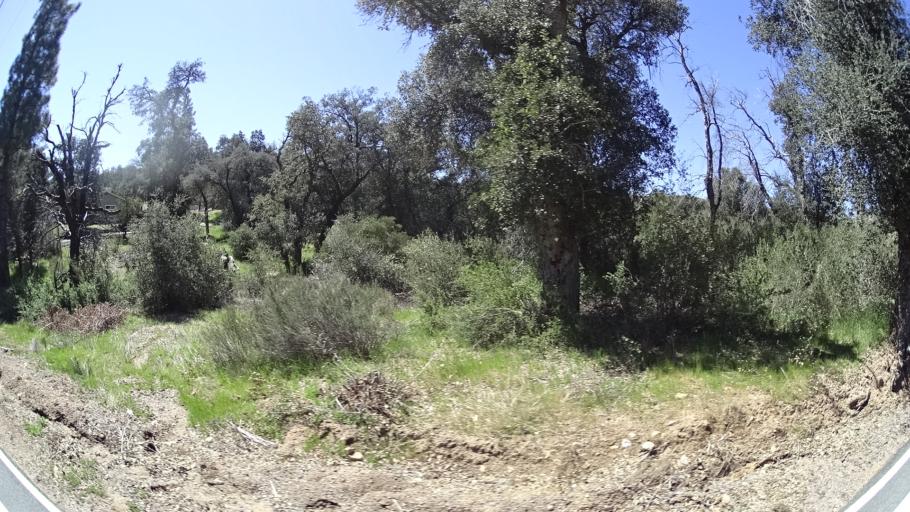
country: US
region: California
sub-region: San Diego County
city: Descanso
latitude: 32.8904
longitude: -116.5764
